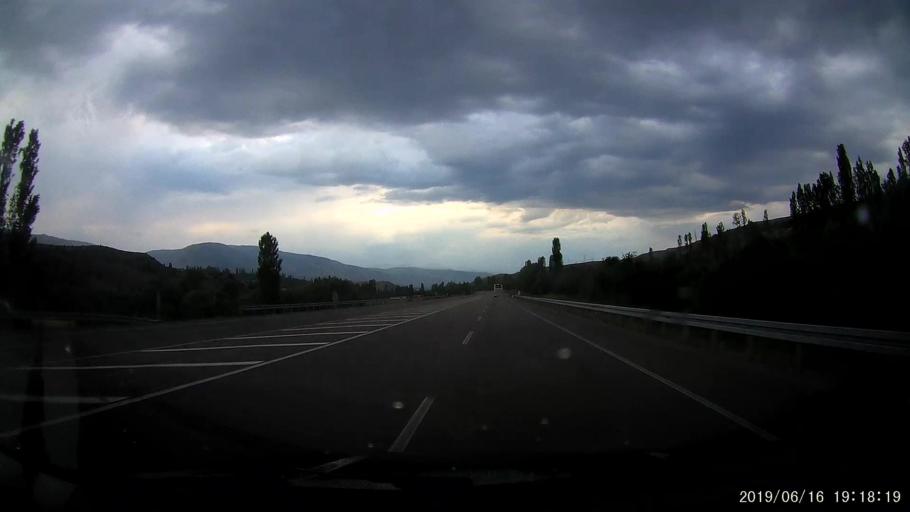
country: TR
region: Sivas
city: Akincilar
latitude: 40.0951
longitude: 38.4615
